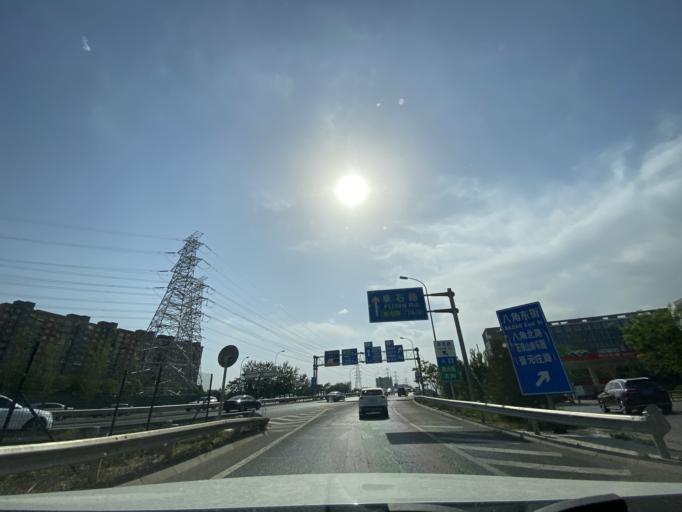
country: CN
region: Beijing
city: Lugu
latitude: 39.9237
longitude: 116.2033
